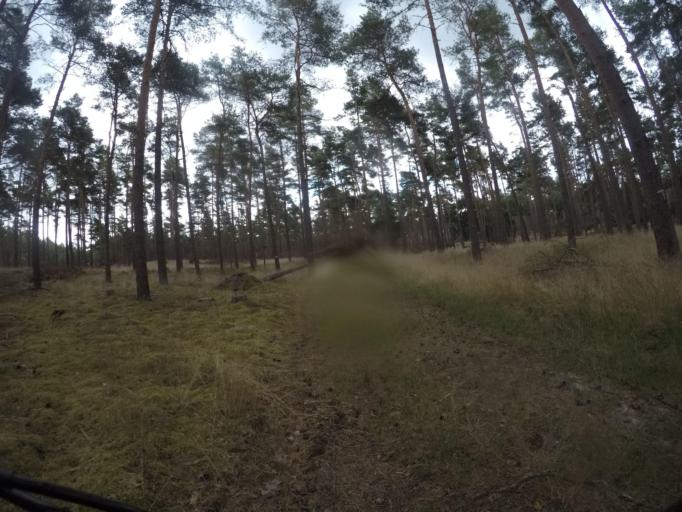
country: DE
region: Lower Saxony
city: Hitzacker
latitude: 53.1923
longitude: 11.0621
